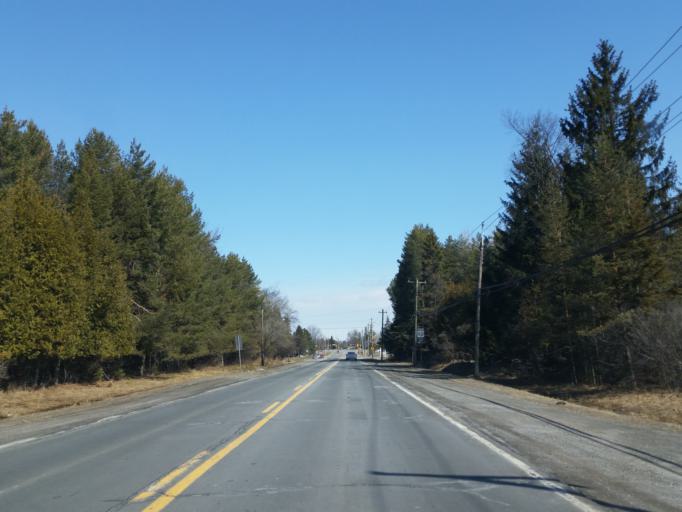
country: CA
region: Ontario
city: Bells Corners
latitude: 45.3081
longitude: -75.8303
